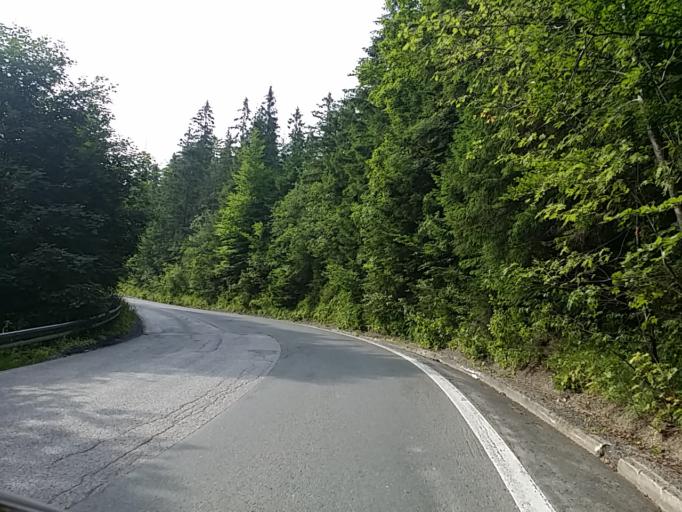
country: SK
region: Kosicky
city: Dobsina
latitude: 48.8966
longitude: 20.2457
